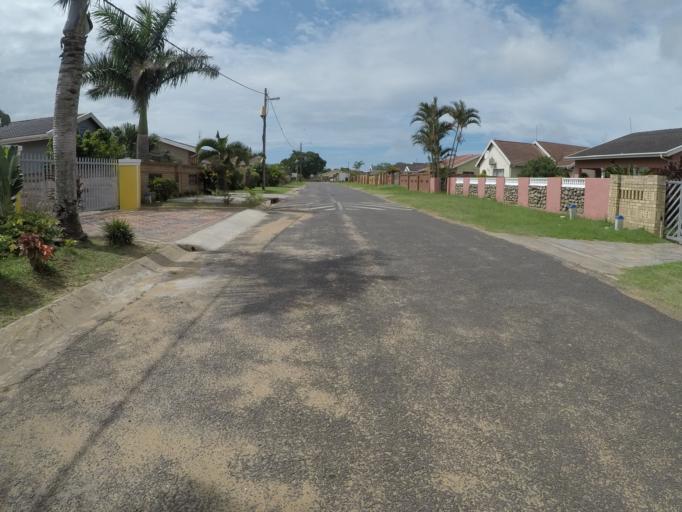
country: ZA
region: KwaZulu-Natal
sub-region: uThungulu District Municipality
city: eSikhawini
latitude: -28.8639
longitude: 31.9140
